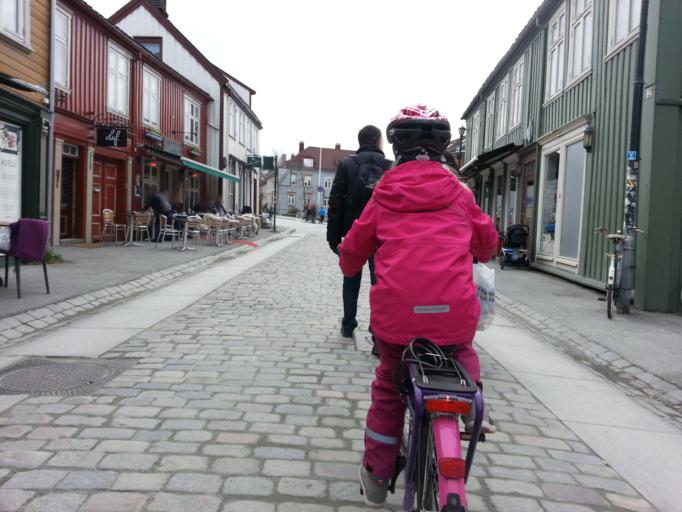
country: NO
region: Sor-Trondelag
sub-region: Trondheim
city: Trondheim
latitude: 63.4284
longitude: 10.4031
